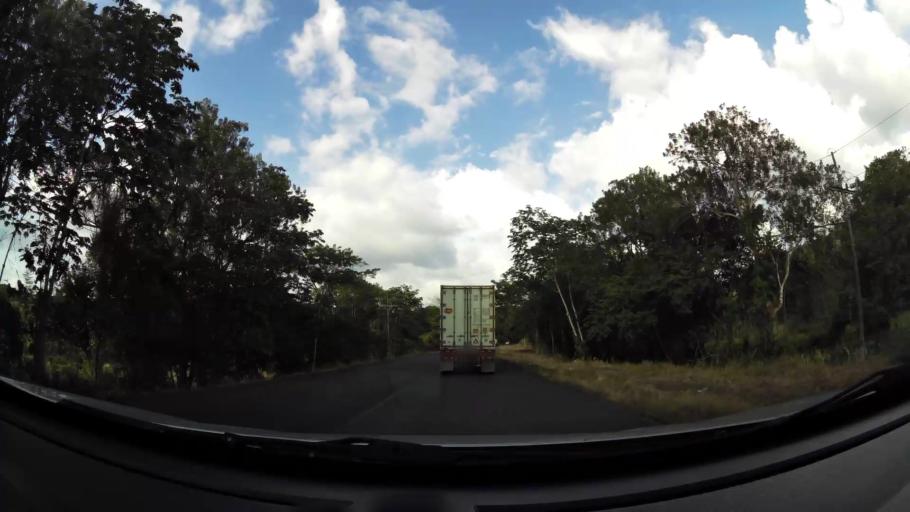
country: CR
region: Puntarenas
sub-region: Canton de Garabito
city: Jaco
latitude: 9.7648
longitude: -84.6140
